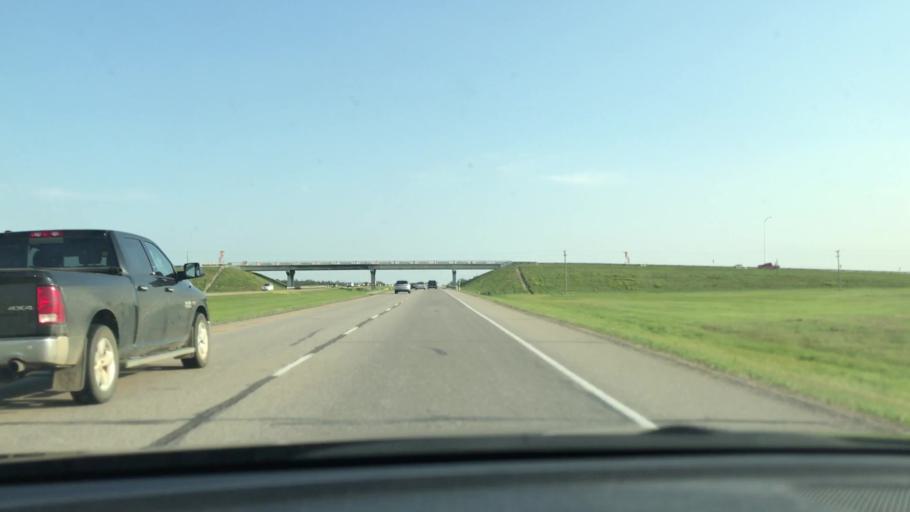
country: CA
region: Alberta
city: Millet
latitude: 53.0928
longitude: -113.5983
